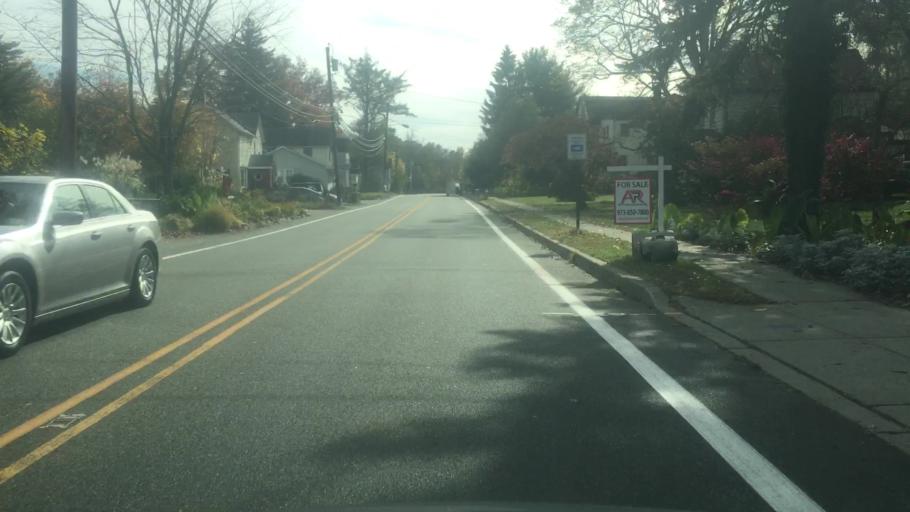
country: US
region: New Jersey
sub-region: Morris County
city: Butler
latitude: 41.0126
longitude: -74.3357
